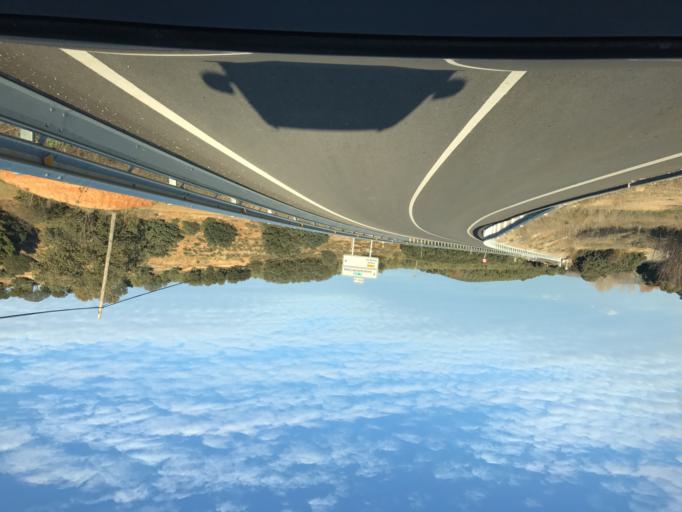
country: ES
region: Andalusia
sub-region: Provincia de Granada
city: Iznalloz
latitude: 37.4117
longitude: -3.4898
